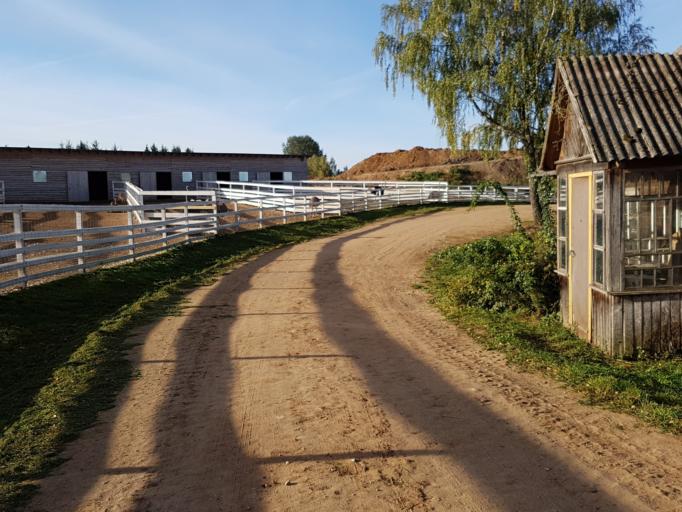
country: LT
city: Moletai
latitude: 55.0358
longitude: 25.4160
